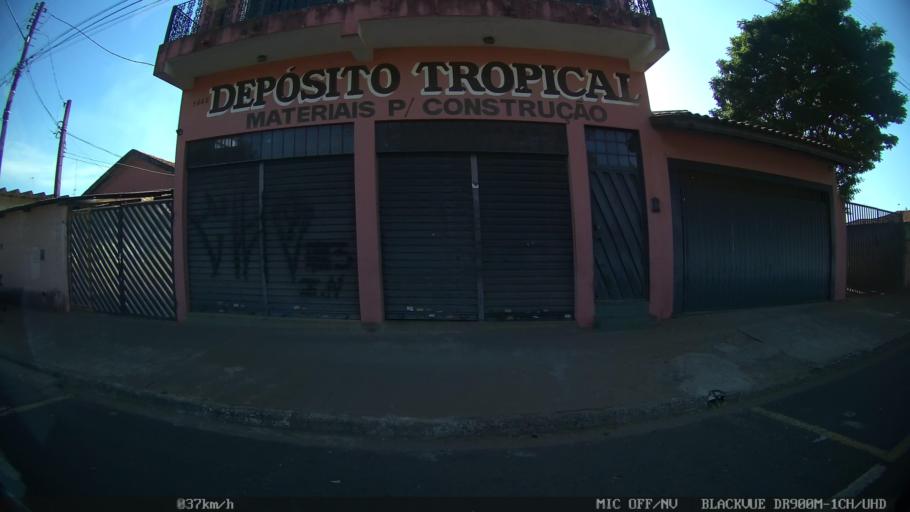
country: BR
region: Sao Paulo
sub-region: Franca
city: Franca
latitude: -20.5011
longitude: -47.4169
